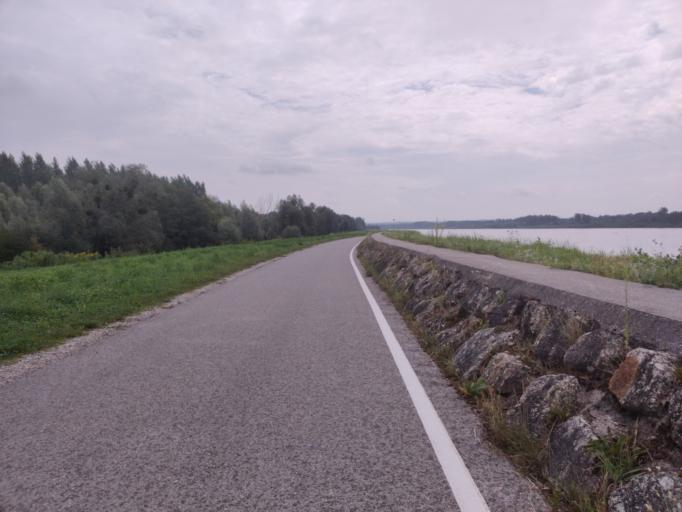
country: AT
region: Upper Austria
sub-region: Politischer Bezirk Perg
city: Perg
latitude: 48.2129
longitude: 14.5977
